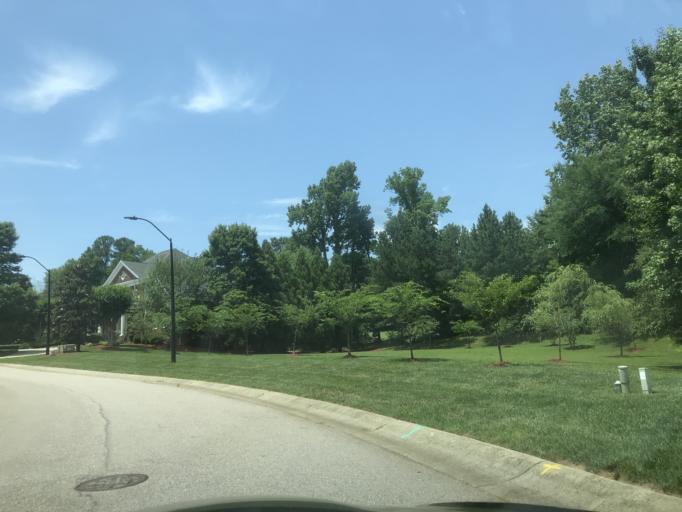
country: US
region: North Carolina
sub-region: Wake County
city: Wake Forest
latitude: 35.9626
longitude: -78.5577
